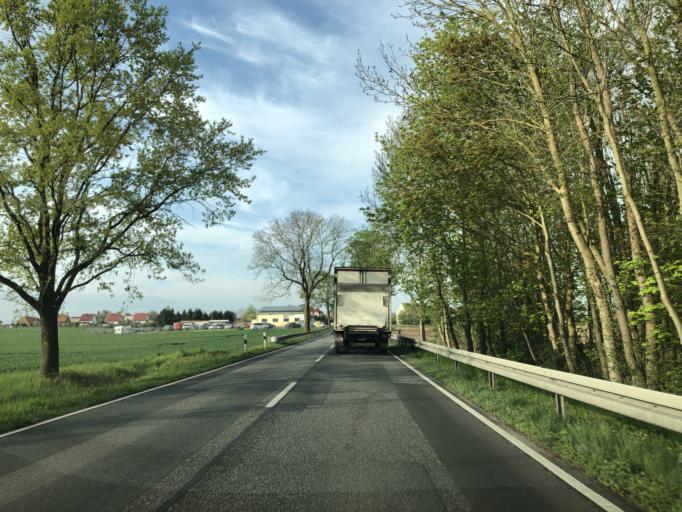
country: DE
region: Mecklenburg-Vorpommern
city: Guestrow
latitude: 53.8464
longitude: 12.2210
